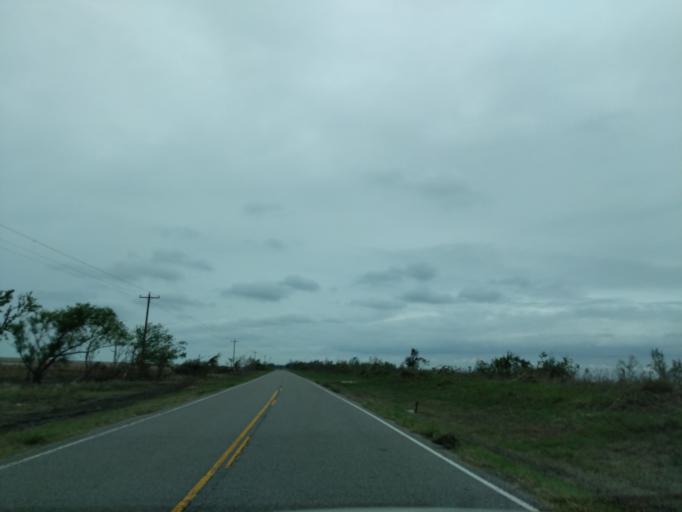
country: US
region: Louisiana
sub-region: Cameron Parish
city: Cameron
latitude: 29.7866
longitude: -93.1667
